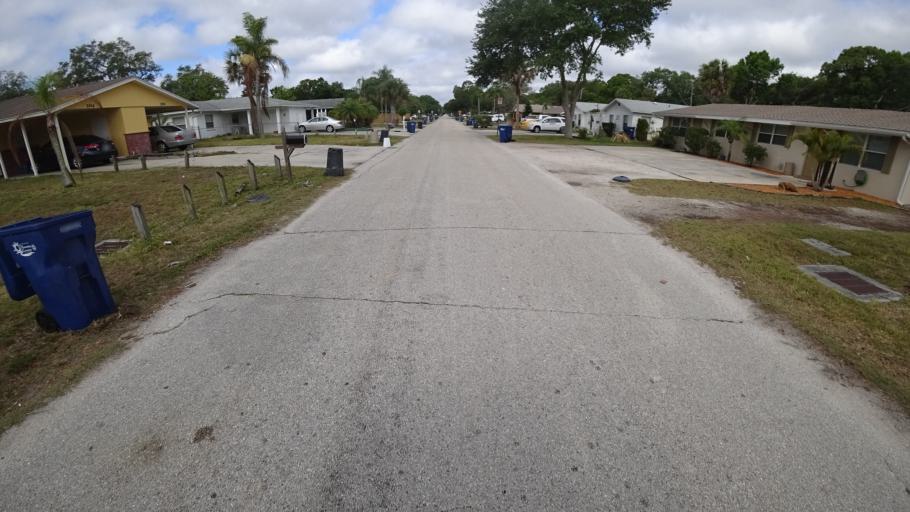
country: US
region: Florida
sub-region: Manatee County
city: South Bradenton
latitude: 27.4492
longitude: -82.5897
